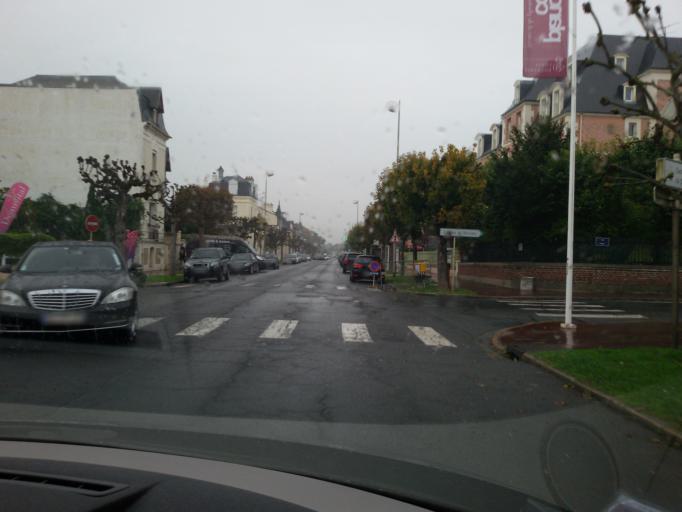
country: FR
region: Lower Normandy
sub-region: Departement du Calvados
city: Deauville
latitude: 49.3575
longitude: 0.0743
